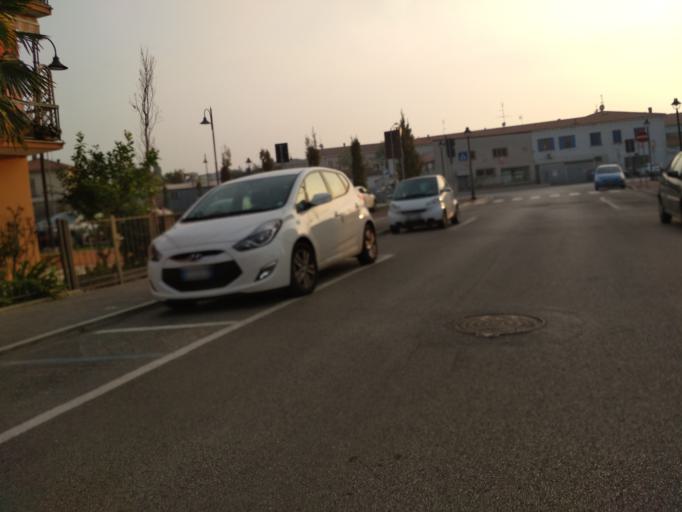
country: IT
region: Emilia-Romagna
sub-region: Provincia di Rimini
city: Rimini
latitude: 44.0558
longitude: 12.5644
